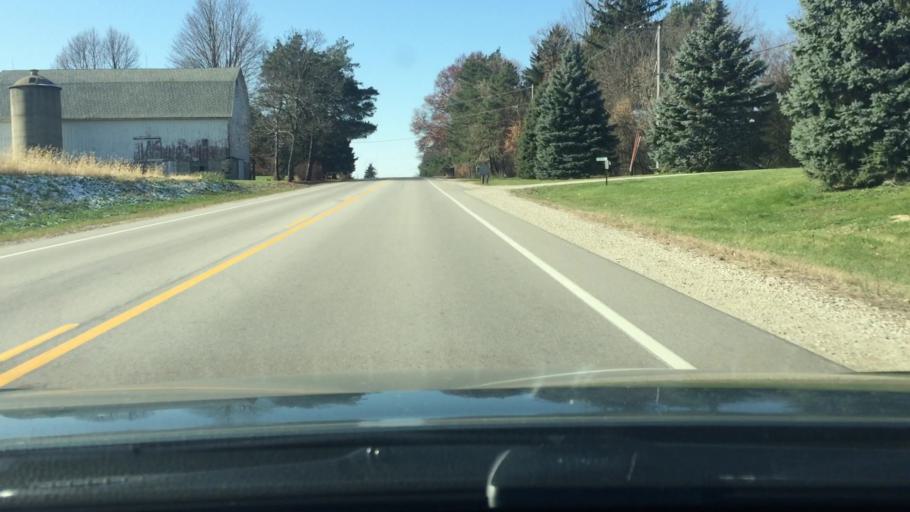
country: US
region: Wisconsin
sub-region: Jefferson County
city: Lake Ripley
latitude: 43.0120
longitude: -88.9821
